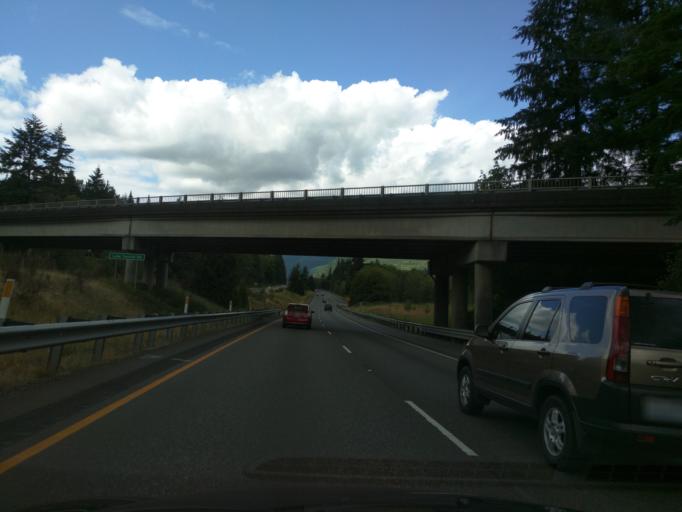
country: US
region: Washington
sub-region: Whatcom County
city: Sudden Valley
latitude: 48.6209
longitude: -122.3563
